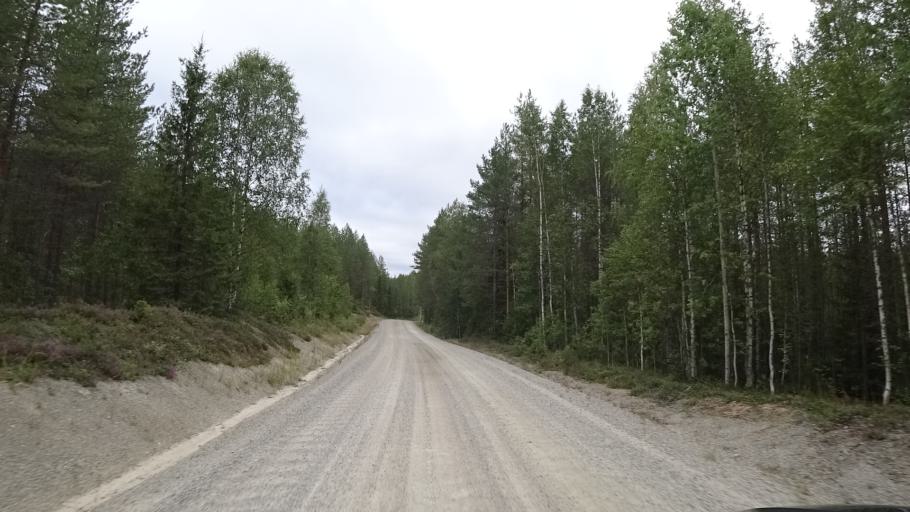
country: FI
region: North Karelia
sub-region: Pielisen Karjala
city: Lieksa
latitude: 63.2410
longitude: 30.3495
